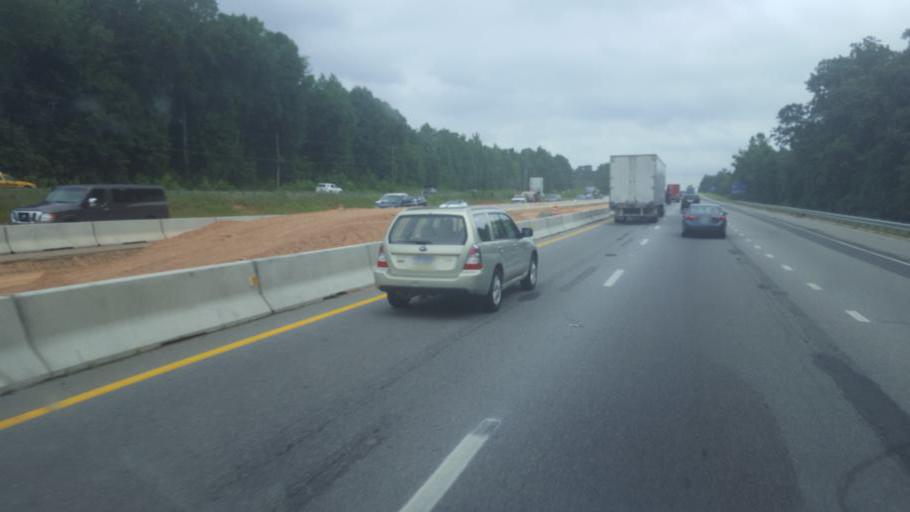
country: US
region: North Carolina
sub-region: Gaston County
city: Davidson
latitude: 35.5435
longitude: -80.8593
